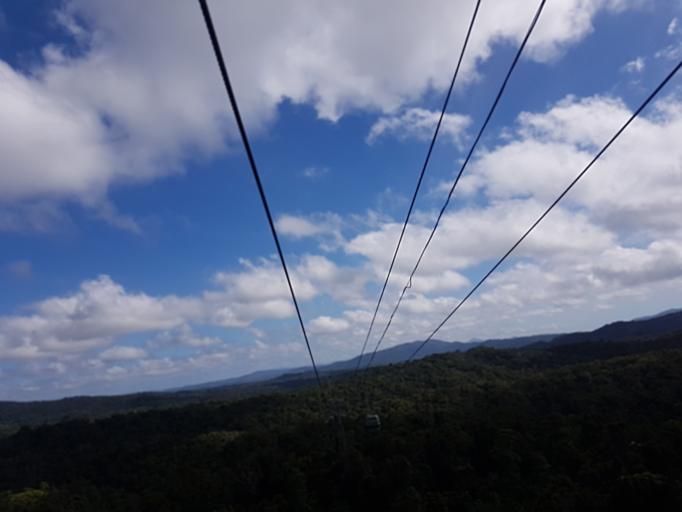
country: AU
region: Queensland
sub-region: Tablelands
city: Kuranda
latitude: -16.8450
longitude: 145.6630
